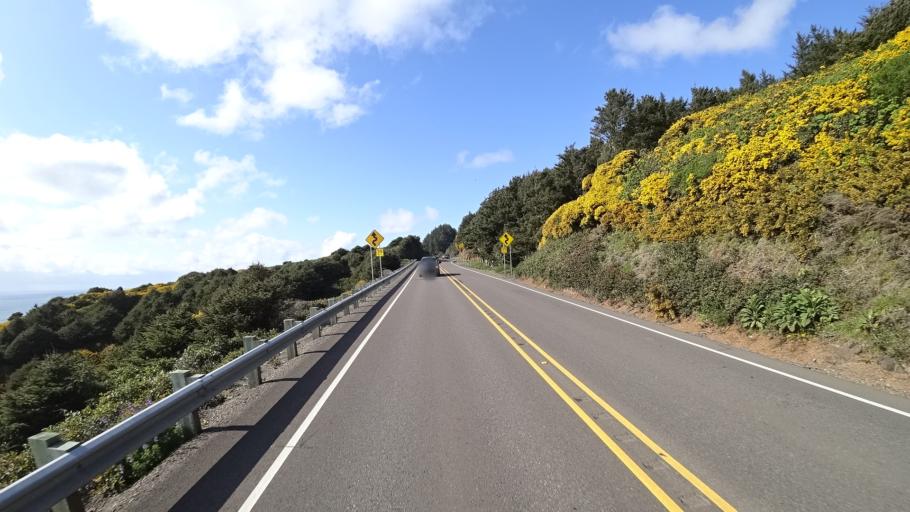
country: US
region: Oregon
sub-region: Lane County
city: Florence
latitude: 44.1100
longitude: -124.1232
